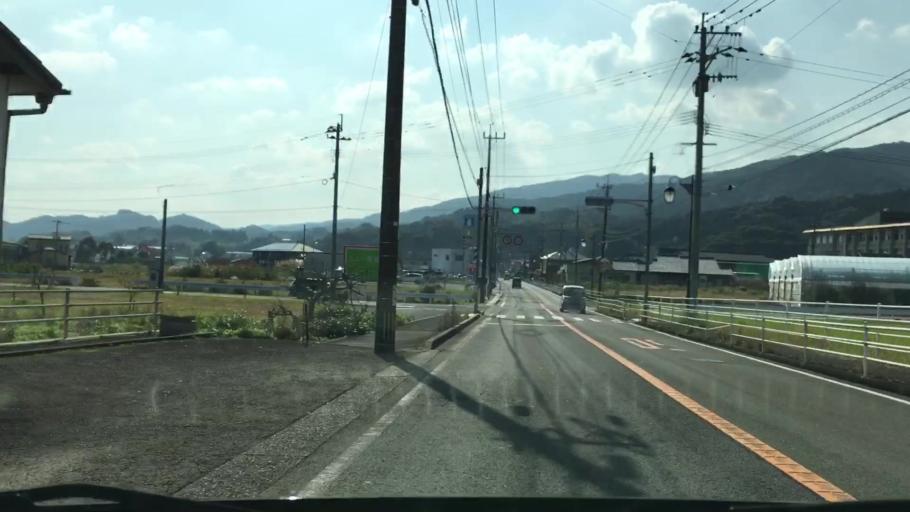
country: JP
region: Nagasaki
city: Togitsu
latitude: 32.9490
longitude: 129.7847
